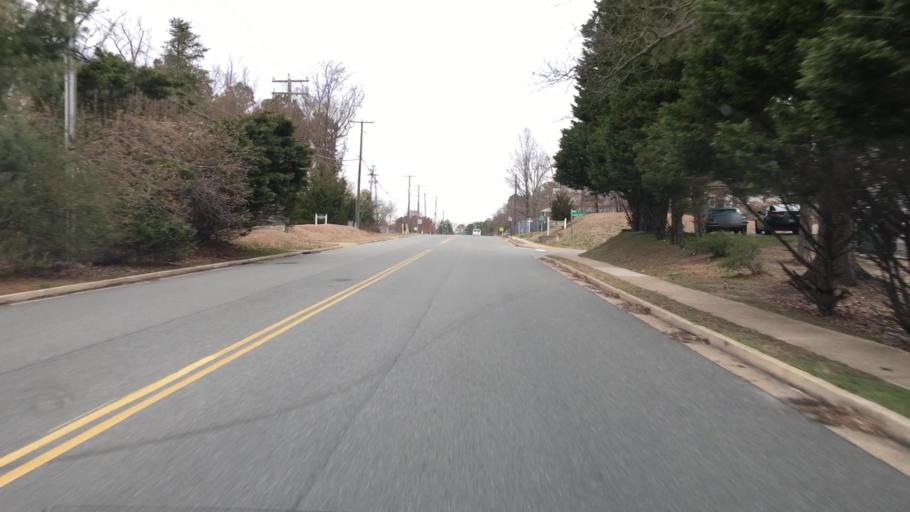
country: US
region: Virginia
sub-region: Henrico County
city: Glen Allen
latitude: 37.6630
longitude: -77.5439
